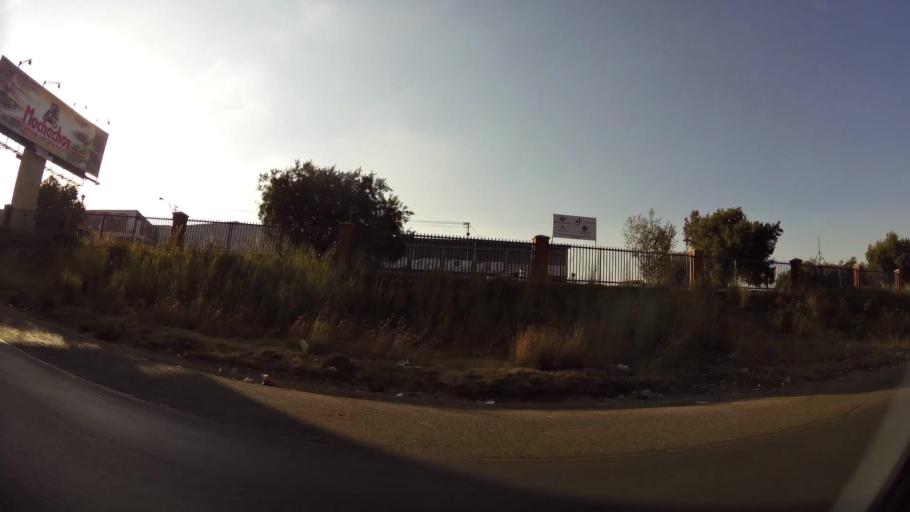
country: ZA
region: Gauteng
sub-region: City of Johannesburg Metropolitan Municipality
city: Johannesburg
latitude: -26.2127
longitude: 28.0860
